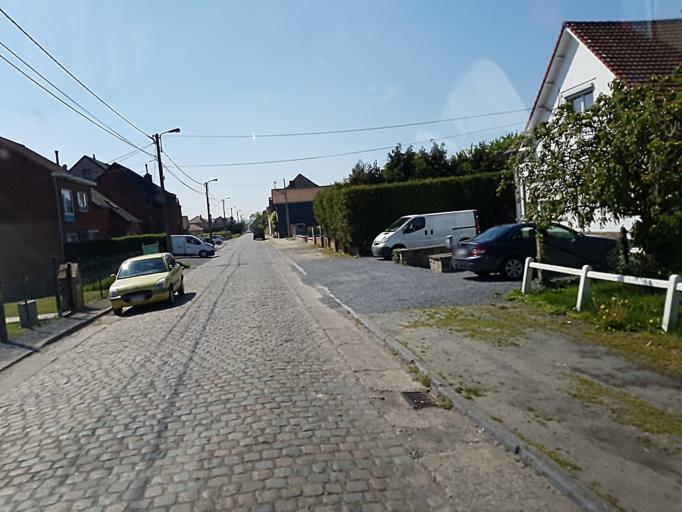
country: BE
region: Wallonia
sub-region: Province du Hainaut
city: Jurbise
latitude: 50.4866
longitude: 3.9074
